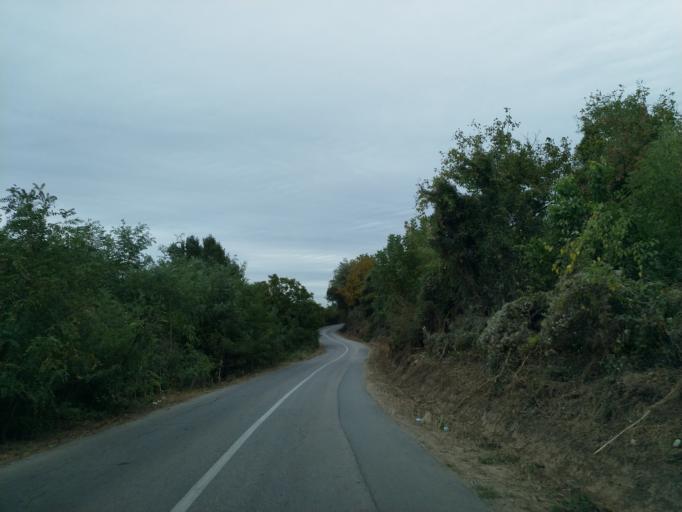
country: RS
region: Central Serbia
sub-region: Pomoravski Okrug
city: Cuprija
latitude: 43.8590
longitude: 21.3248
